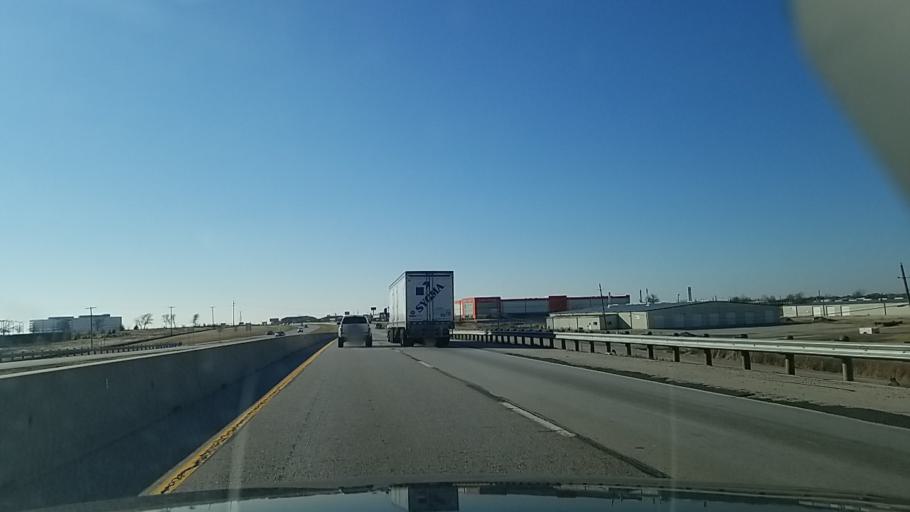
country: US
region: Texas
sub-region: Tarrant County
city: Haslet
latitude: 32.9328
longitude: -97.3157
